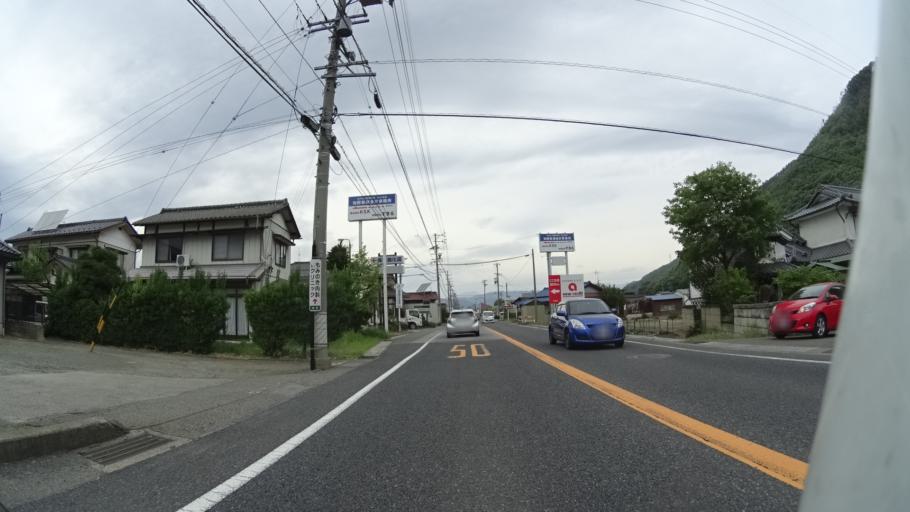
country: JP
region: Nagano
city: Nagano-shi
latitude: 36.5128
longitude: 138.1352
